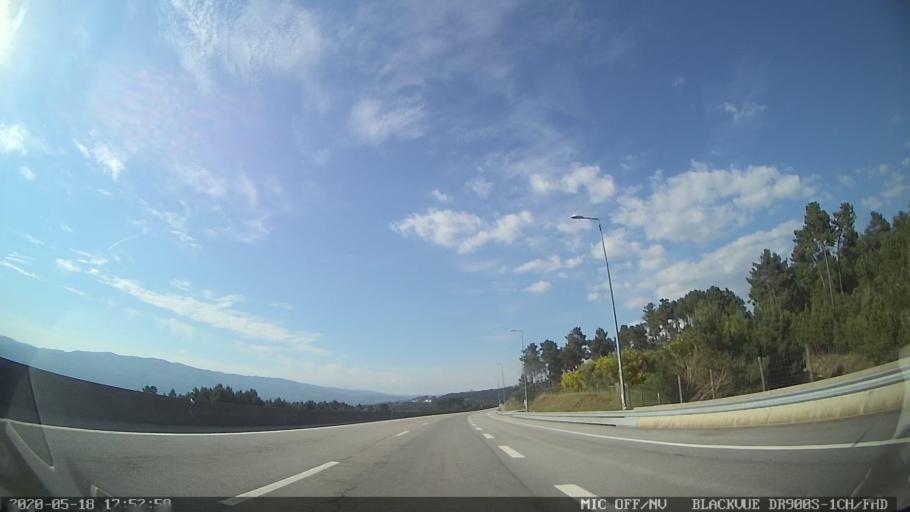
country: PT
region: Vila Real
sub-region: Vila Real
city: Vila Real
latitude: 41.2974
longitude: -7.6956
